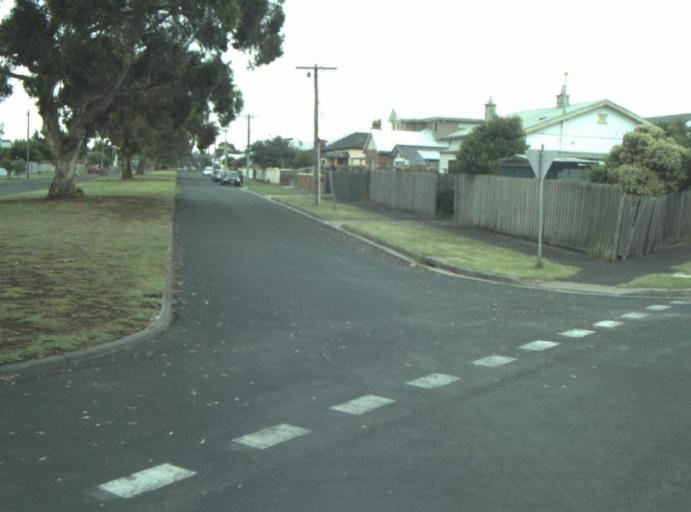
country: AU
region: Victoria
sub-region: Greater Geelong
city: East Geelong
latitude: -38.1615
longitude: 144.3719
